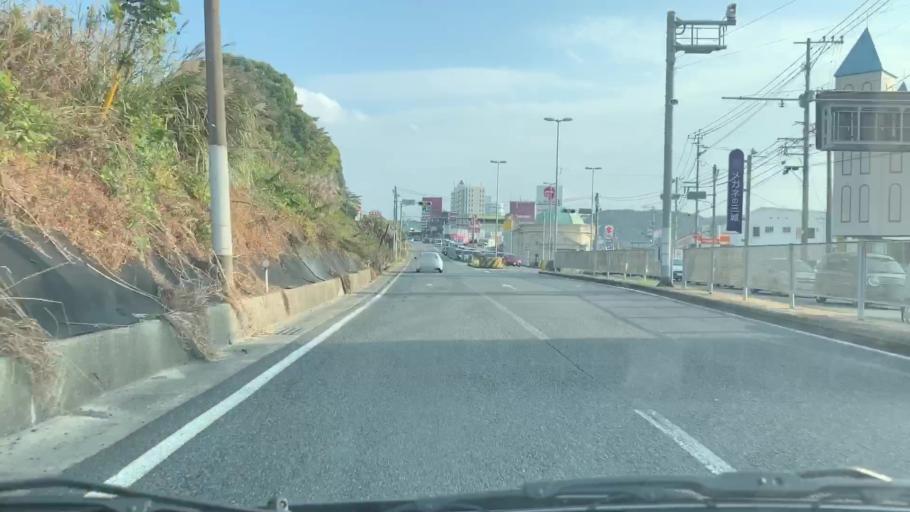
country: JP
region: Nagasaki
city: Sasebo
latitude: 33.1451
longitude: 129.7853
